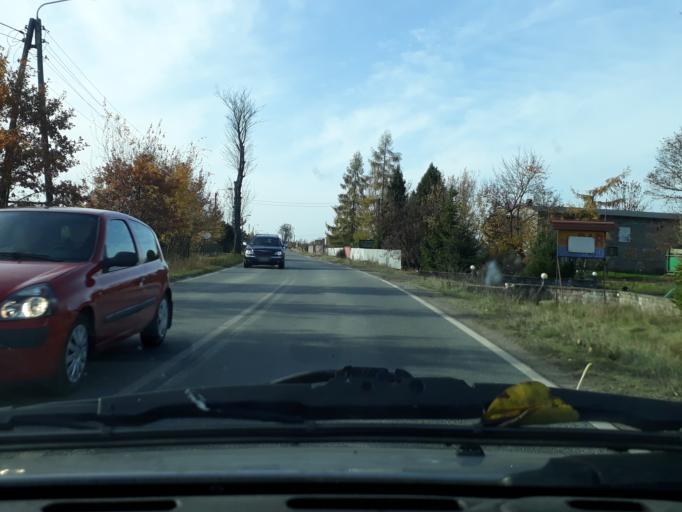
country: PL
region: Silesian Voivodeship
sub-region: Powiat lubliniecki
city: Psary
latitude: 50.5770
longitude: 19.0020
